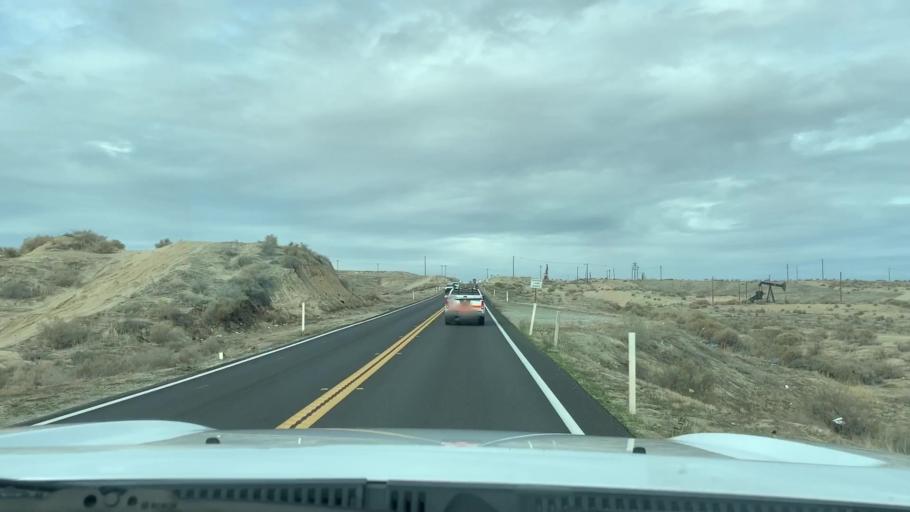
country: US
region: California
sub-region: Kern County
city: South Taft
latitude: 35.1112
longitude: -119.4257
